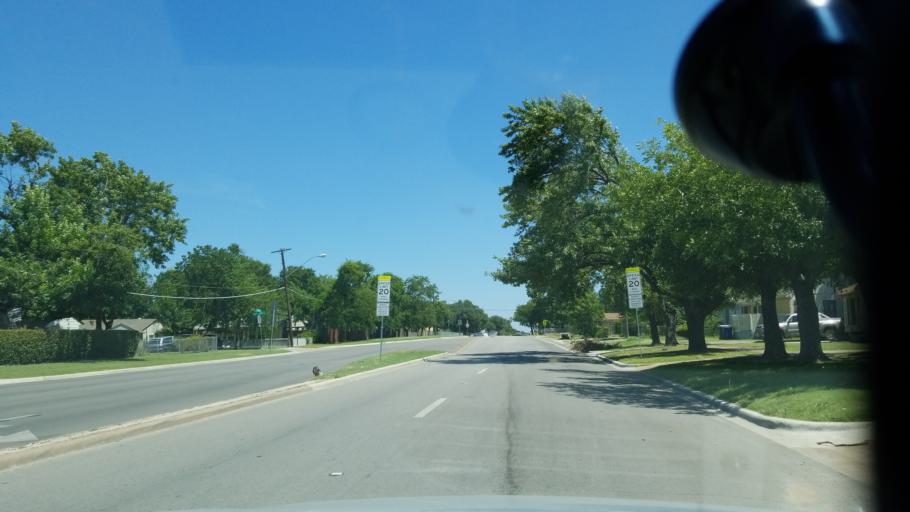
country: US
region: Texas
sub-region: Dallas County
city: Cockrell Hill
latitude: 32.7061
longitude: -96.8229
